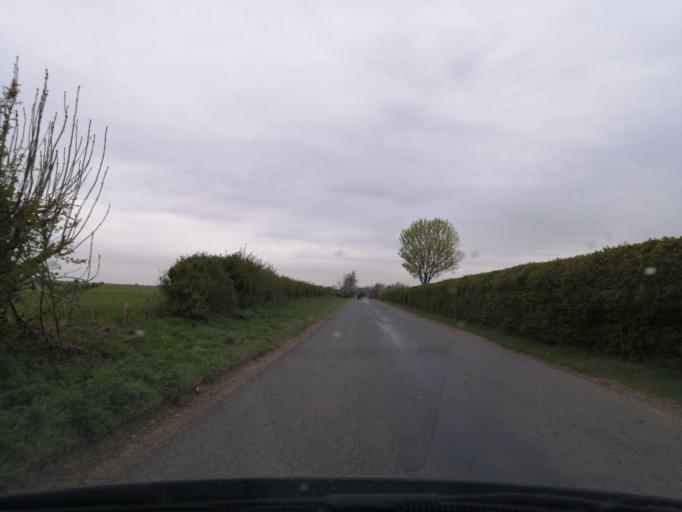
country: GB
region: England
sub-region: Peterborough
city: Wittering
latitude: 52.5961
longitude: -0.4598
